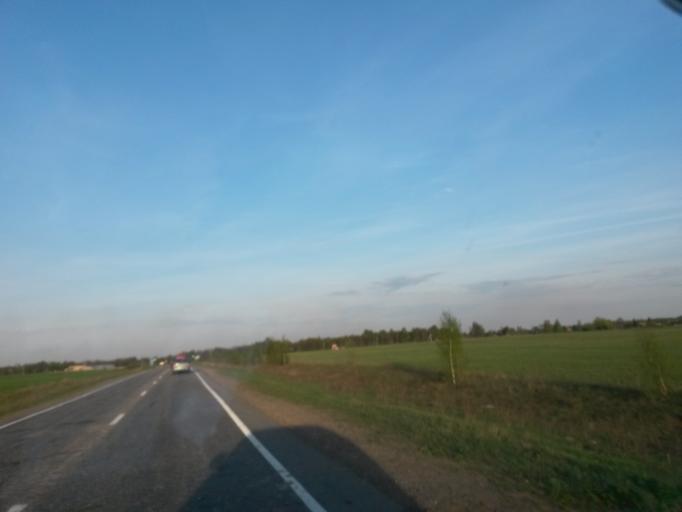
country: RU
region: Jaroslavl
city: Kurba
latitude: 57.6816
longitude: 39.5123
